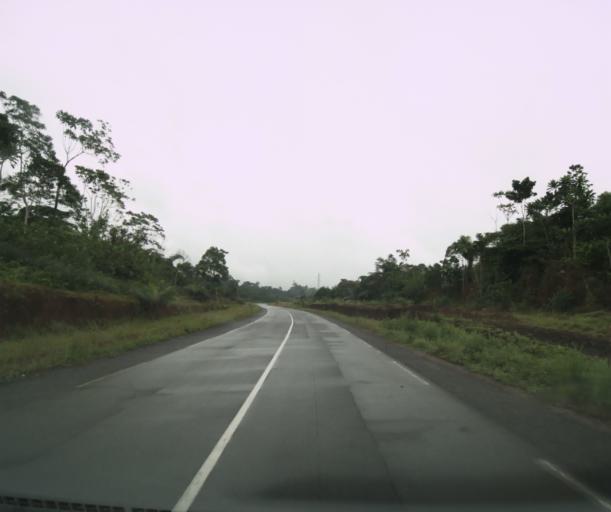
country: CM
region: Littoral
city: Dizangue
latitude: 3.3737
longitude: 10.1028
